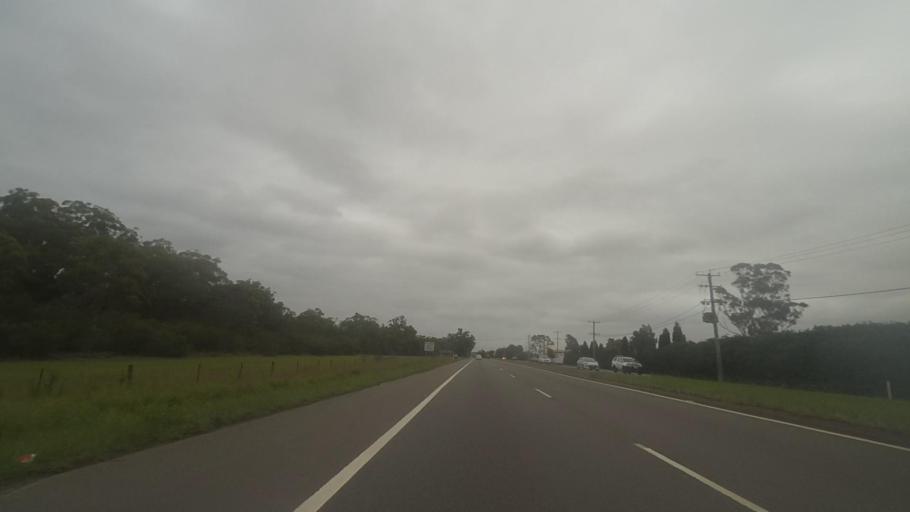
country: AU
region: New South Wales
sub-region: Port Stephens Shire
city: Raymond Terrace
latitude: -32.7972
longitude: 151.7197
